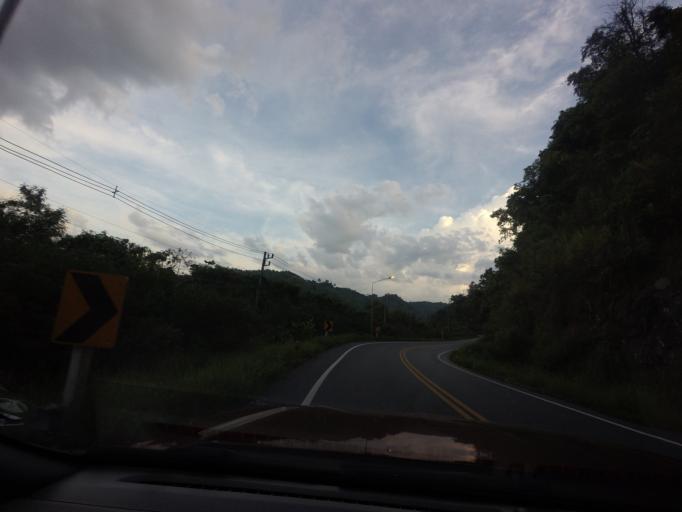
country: TH
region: Yala
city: Than To
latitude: 6.0434
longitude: 101.1984
